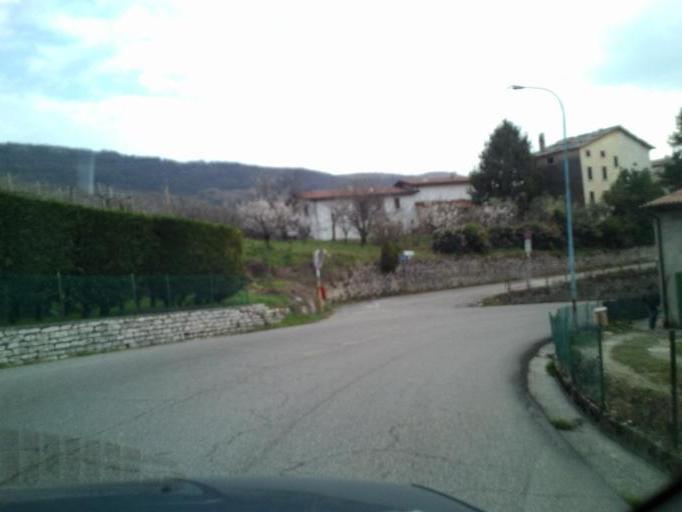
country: IT
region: Veneto
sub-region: Provincia di Verona
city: Fane
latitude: 45.5628
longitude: 10.9592
